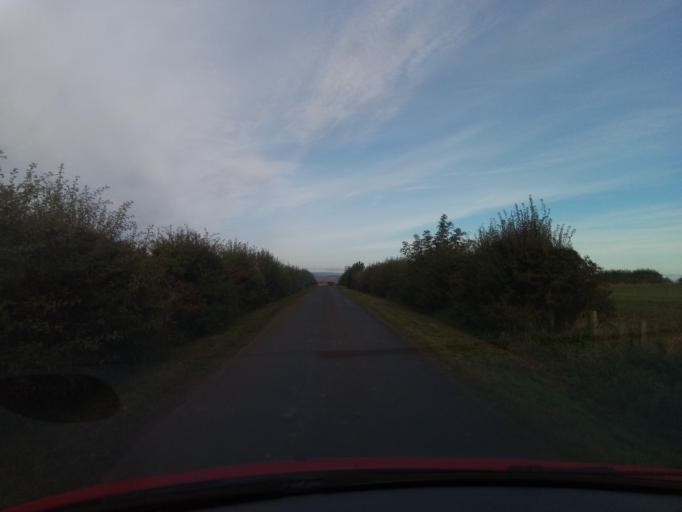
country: GB
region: Scotland
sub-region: The Scottish Borders
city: Kelso
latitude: 55.5859
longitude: -2.3743
